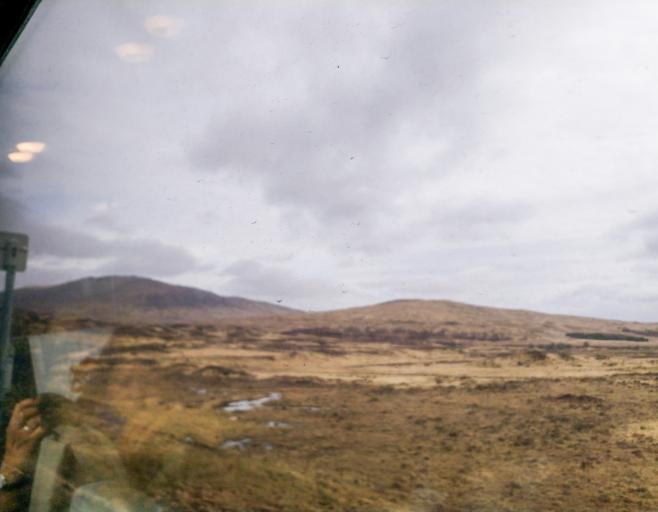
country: GB
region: Scotland
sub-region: Highland
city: Spean Bridge
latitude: 56.6878
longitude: -4.5765
